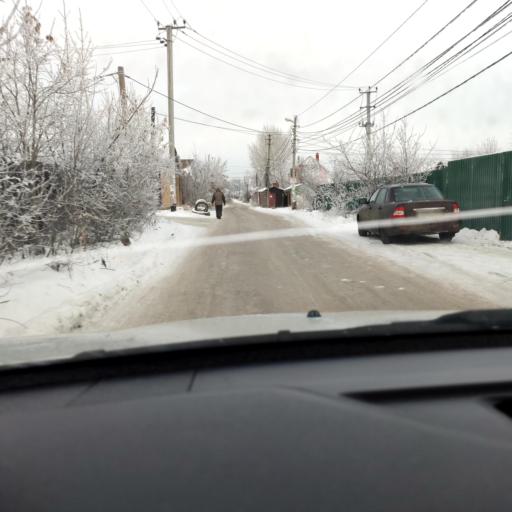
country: RU
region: Samara
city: Petra-Dubrava
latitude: 53.3004
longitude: 50.2516
